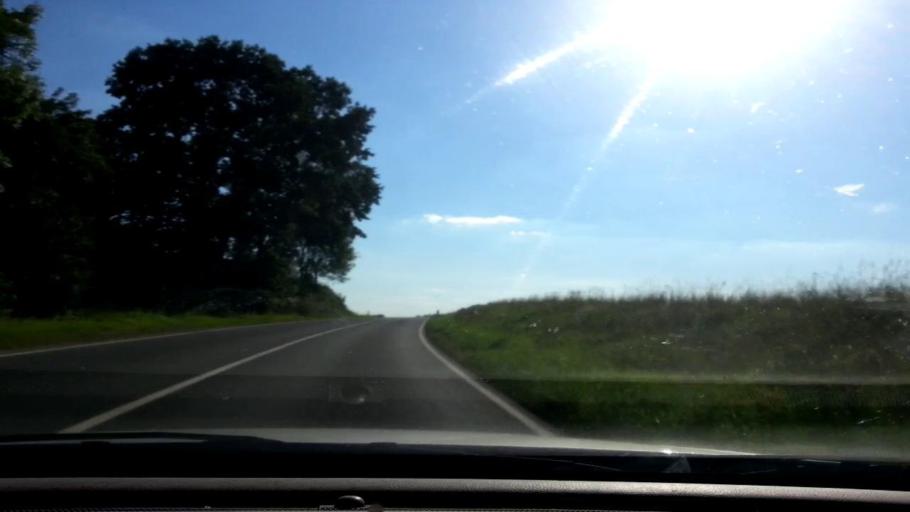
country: DE
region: Bavaria
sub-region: Upper Franconia
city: Schesslitz
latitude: 49.9572
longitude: 10.9958
